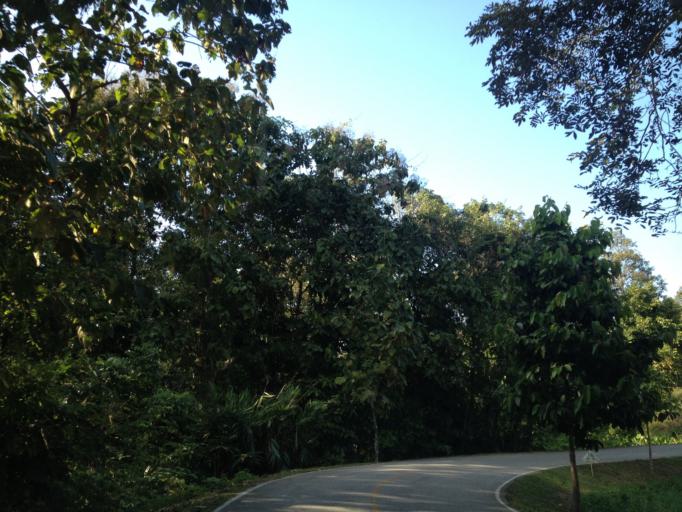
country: TH
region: Chiang Mai
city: Chiang Mai
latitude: 18.8682
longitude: 98.9377
